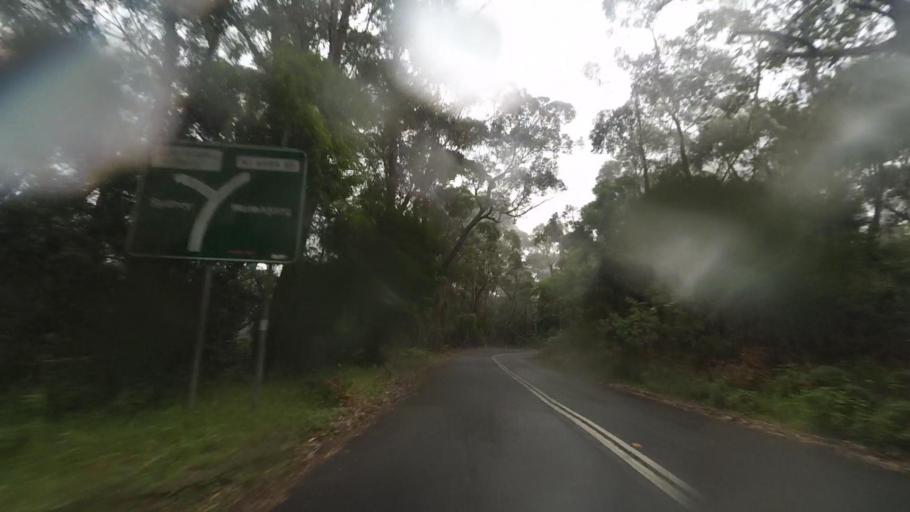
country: AU
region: New South Wales
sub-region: Wollongong
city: Mount Keira
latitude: -34.3925
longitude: 150.8475
